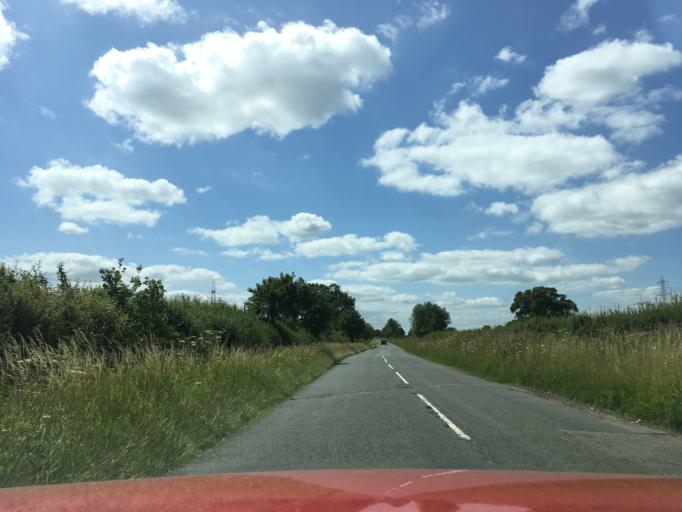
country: GB
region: England
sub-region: Buckinghamshire
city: Winslow
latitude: 51.9292
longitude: -0.8352
